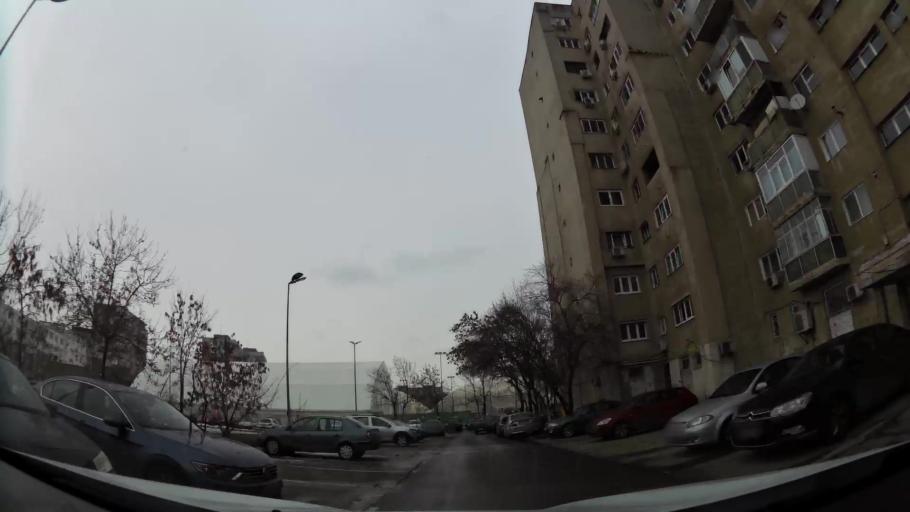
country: RO
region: Ilfov
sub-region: Comuna Chiajna
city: Rosu
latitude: 44.4177
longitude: 26.0327
